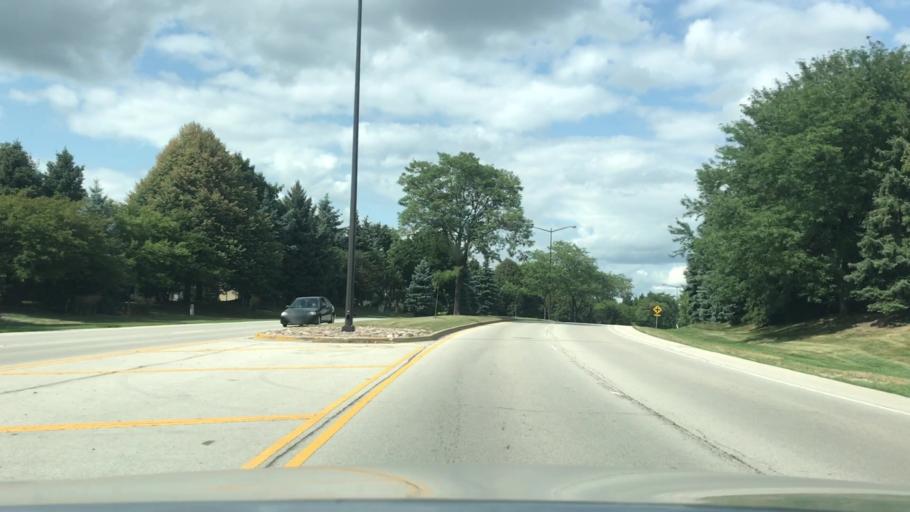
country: US
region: Illinois
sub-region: Kane County
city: Aurora
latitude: 41.7494
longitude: -88.2471
